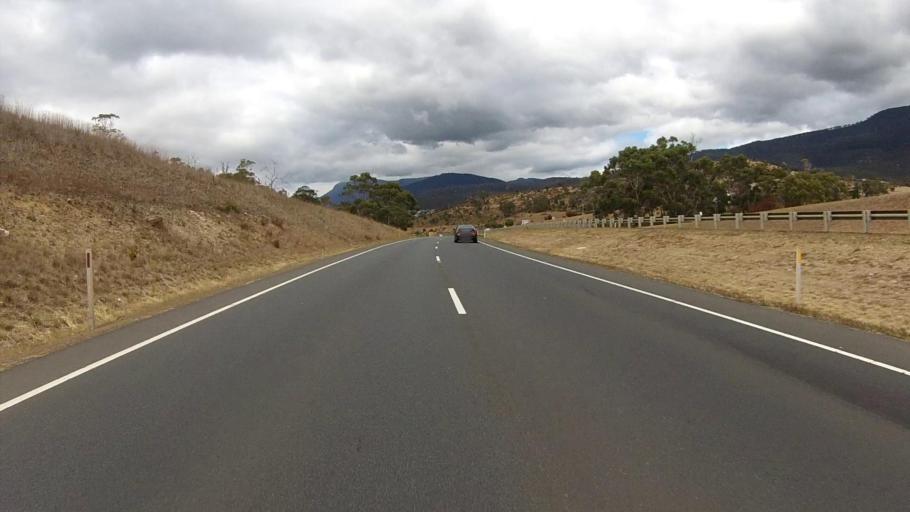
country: AU
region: Tasmania
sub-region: Glenorchy
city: Claremont
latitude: -42.7752
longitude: 147.2391
